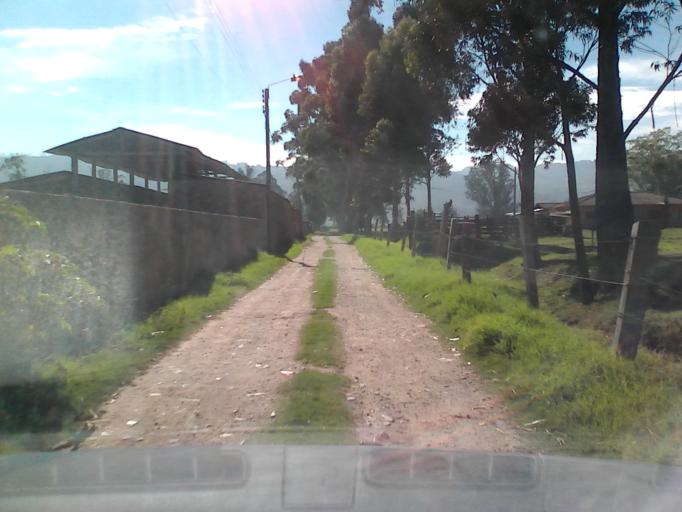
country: CO
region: Boyaca
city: Duitama
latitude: 5.7818
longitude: -73.0398
